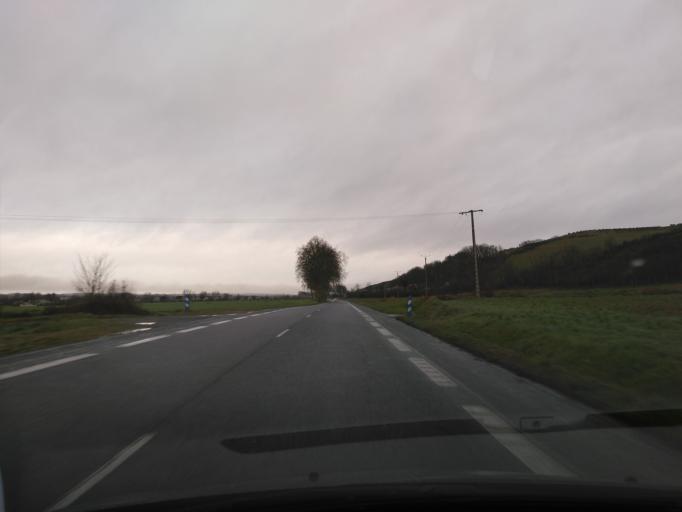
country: FR
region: Midi-Pyrenees
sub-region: Departement de la Haute-Garonne
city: Montesquieu-Volvestre
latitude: 43.2257
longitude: 1.2111
